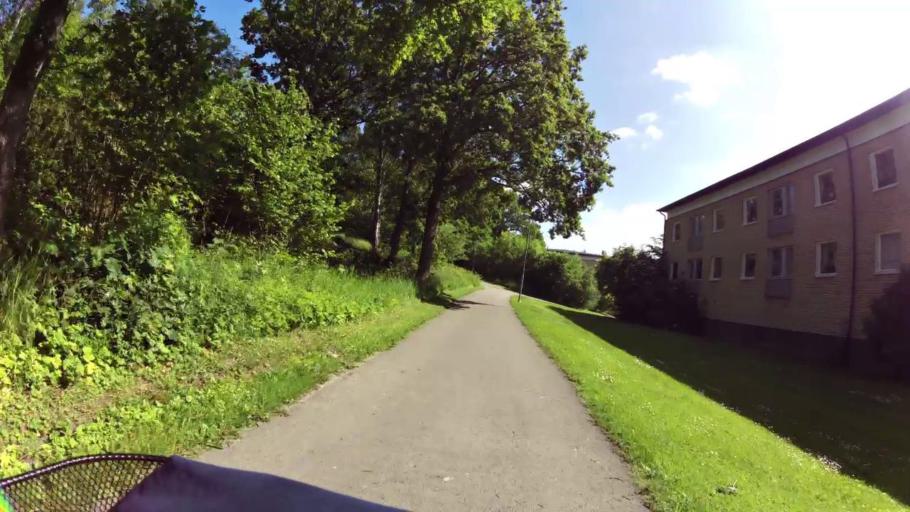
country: SE
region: OEstergoetland
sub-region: Linkopings Kommun
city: Linkoping
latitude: 58.3854
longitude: 15.6388
